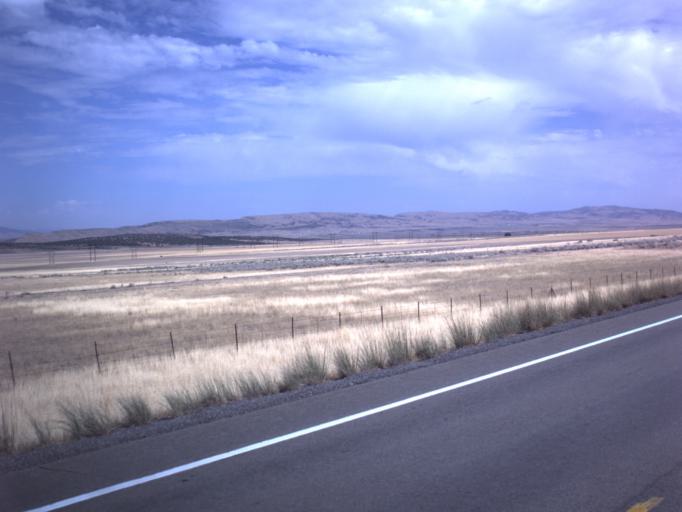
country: US
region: Utah
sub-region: Sanpete County
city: Gunnison
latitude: 39.4259
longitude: -111.9201
